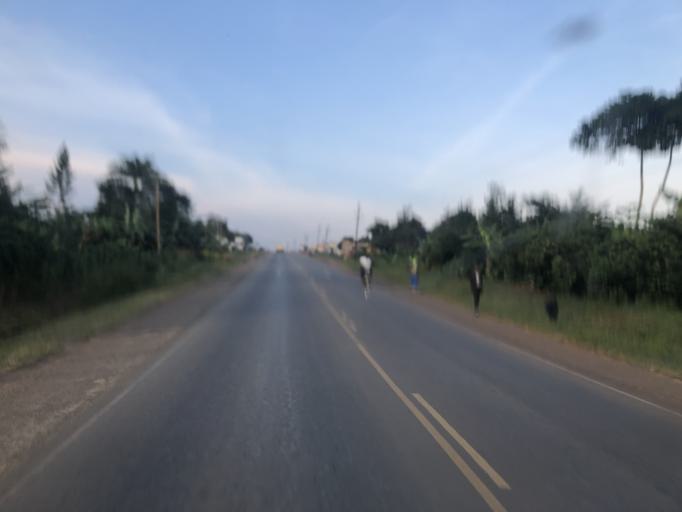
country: UG
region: Central Region
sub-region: Mpigi District
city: Mpigi
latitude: 0.2053
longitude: 32.3120
